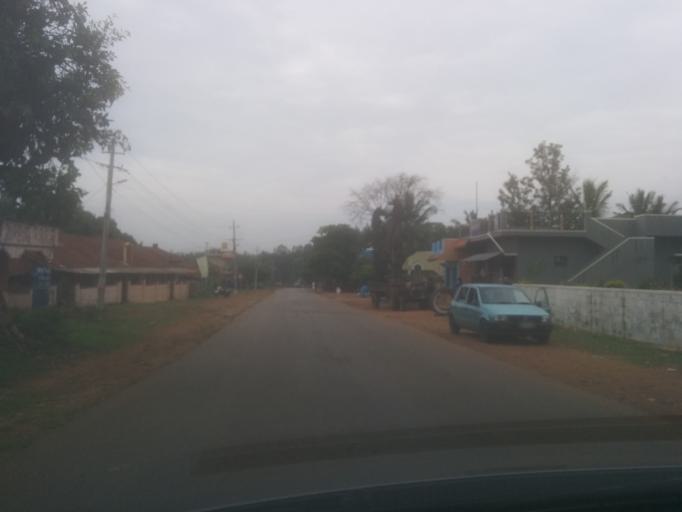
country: IN
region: Karnataka
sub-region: Chikmagalur
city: Chikmagalur
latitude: 13.3559
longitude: 75.7589
